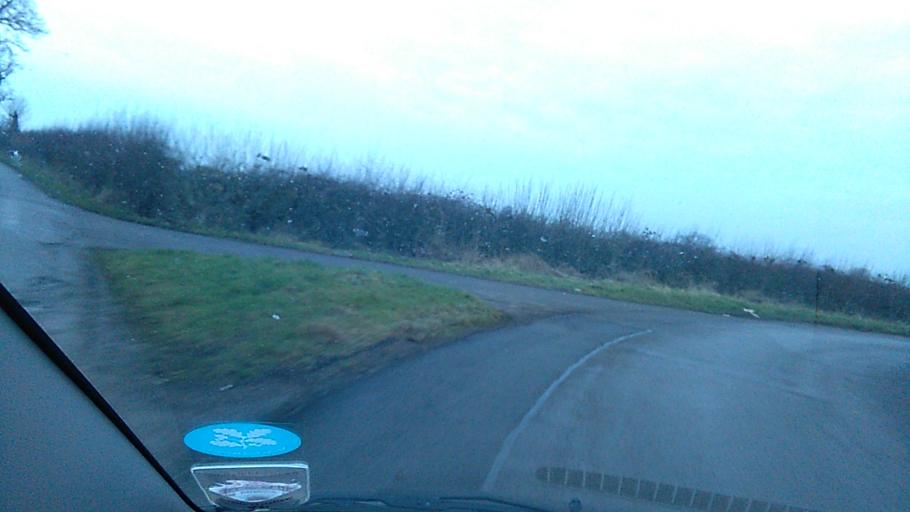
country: GB
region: England
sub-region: Leicestershire
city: Melton Mowbray
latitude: 52.7958
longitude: -0.8913
